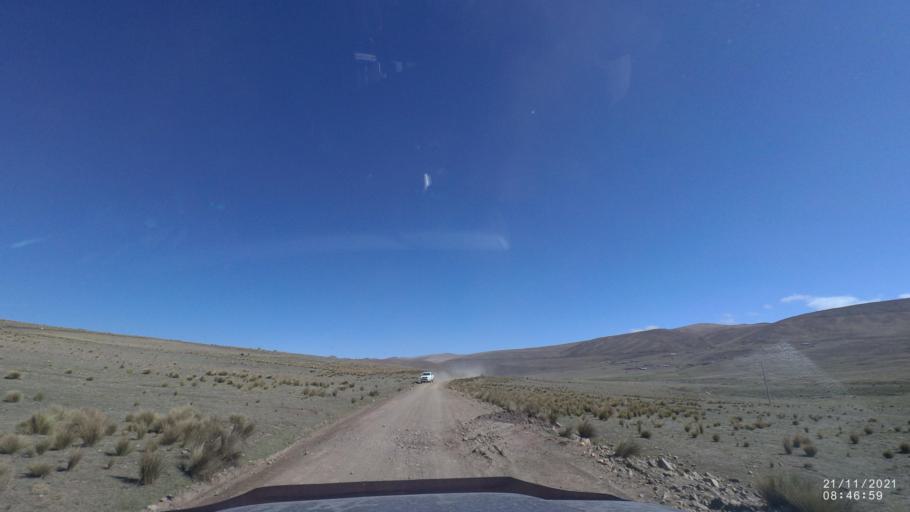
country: BO
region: Cochabamba
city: Cochabamba
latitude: -17.2391
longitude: -66.2333
